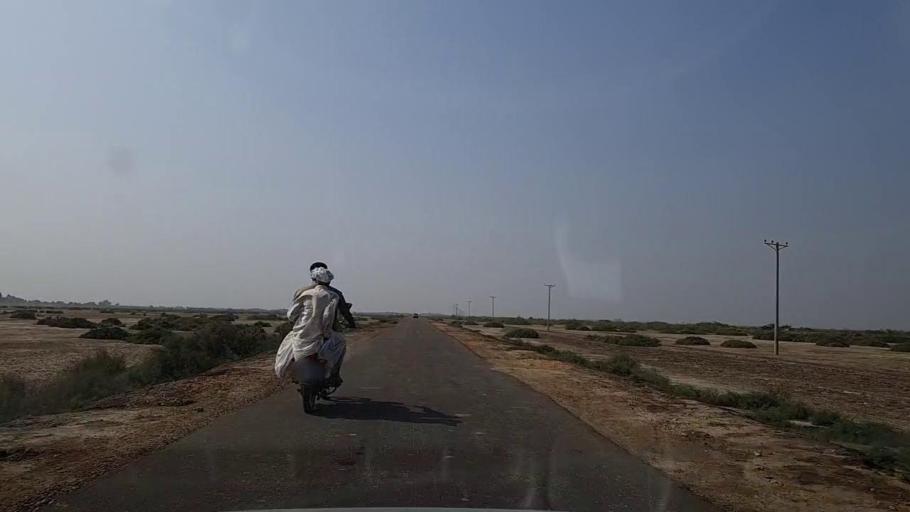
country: PK
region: Sindh
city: Mirpur Sakro
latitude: 24.5289
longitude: 67.5813
